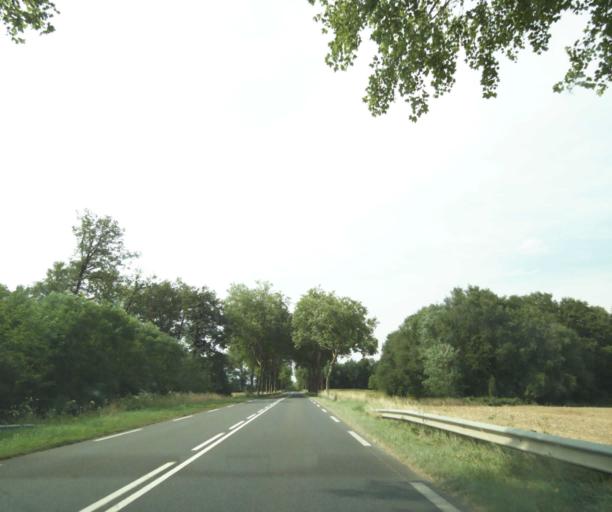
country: FR
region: Centre
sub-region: Departement d'Indre-et-Loire
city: Neuille-Pont-Pierre
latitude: 47.5763
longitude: 0.5439
